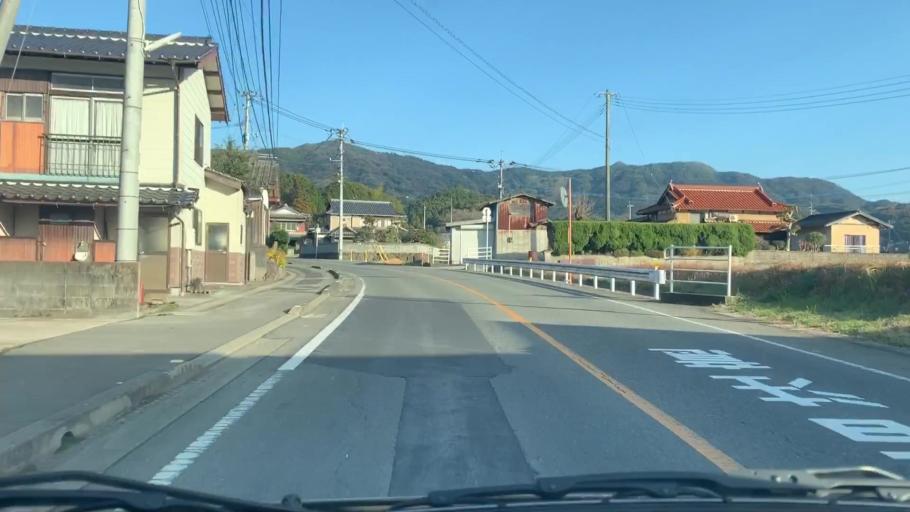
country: JP
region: Saga Prefecture
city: Takeocho-takeo
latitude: 33.2244
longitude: 130.0256
